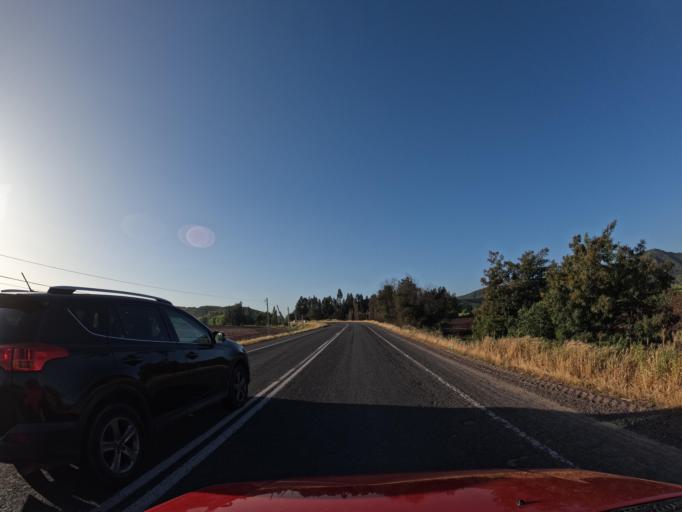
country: CL
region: O'Higgins
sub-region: Provincia de Colchagua
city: Santa Cruz
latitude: -34.4338
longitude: -71.3692
